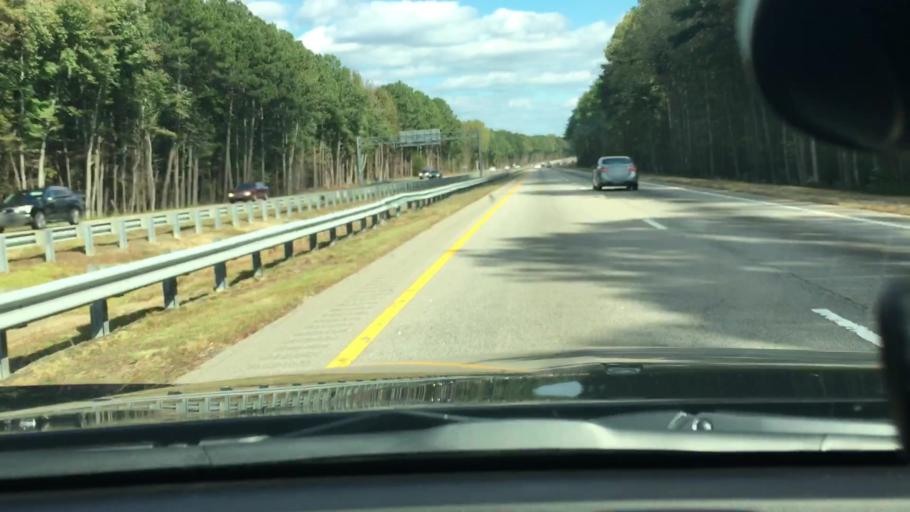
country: US
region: North Carolina
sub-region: Wake County
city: Wendell
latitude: 35.8192
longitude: -78.3935
